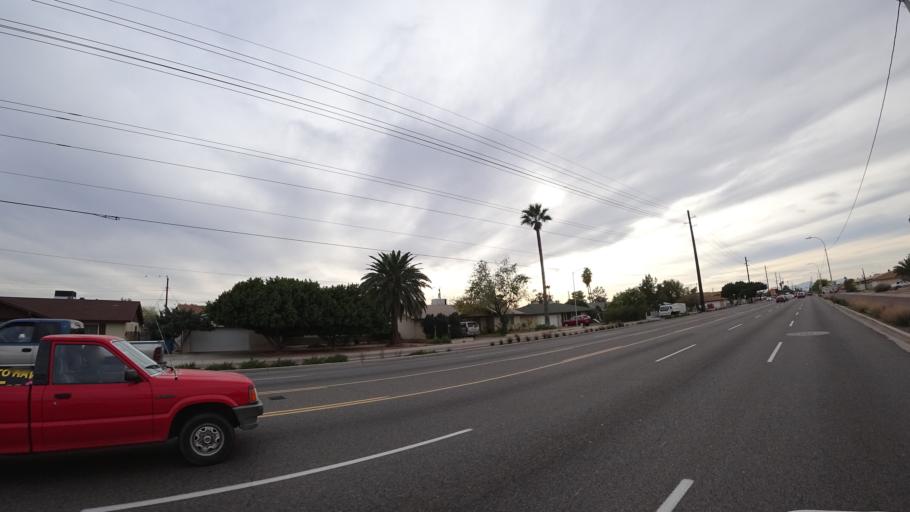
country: US
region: Arizona
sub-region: Maricopa County
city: Glendale
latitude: 33.5676
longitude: -112.1472
